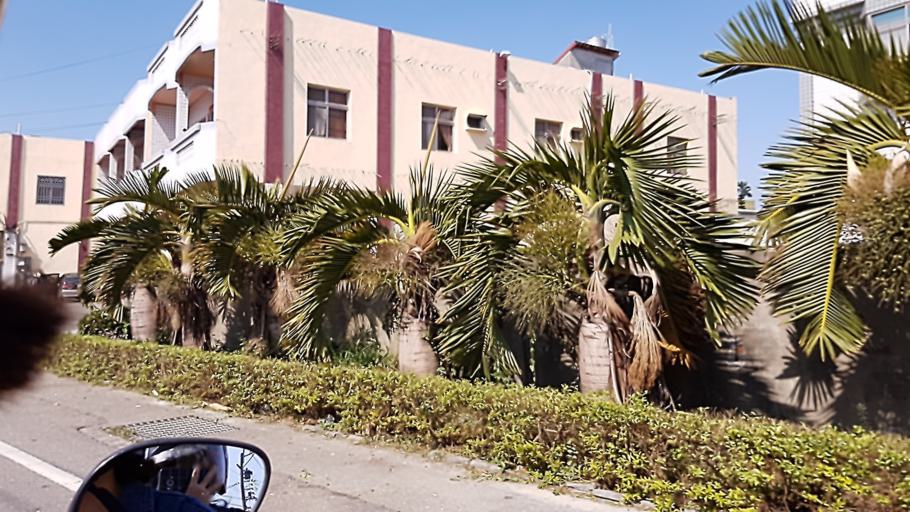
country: TW
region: Taiwan
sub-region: Changhua
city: Chang-hua
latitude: 24.0814
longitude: 120.5006
